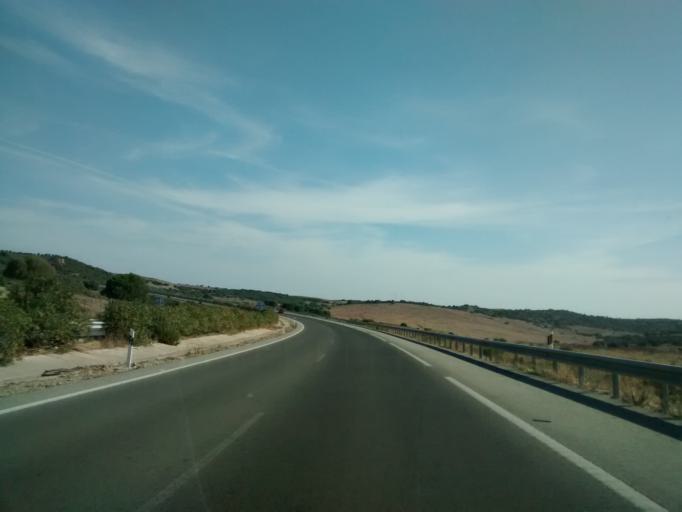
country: ES
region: Andalusia
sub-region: Provincia de Cadiz
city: Conil de la Frontera
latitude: 36.3335
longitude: -6.0501
